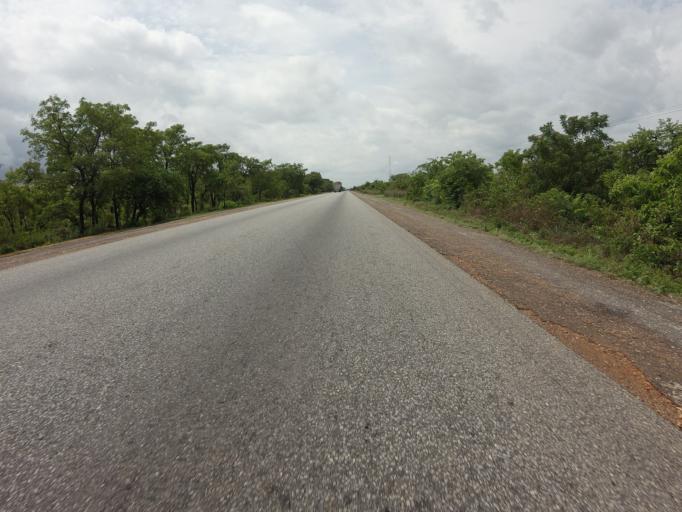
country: GH
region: Brong-Ahafo
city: Kintampo
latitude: 8.6900
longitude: -1.5055
